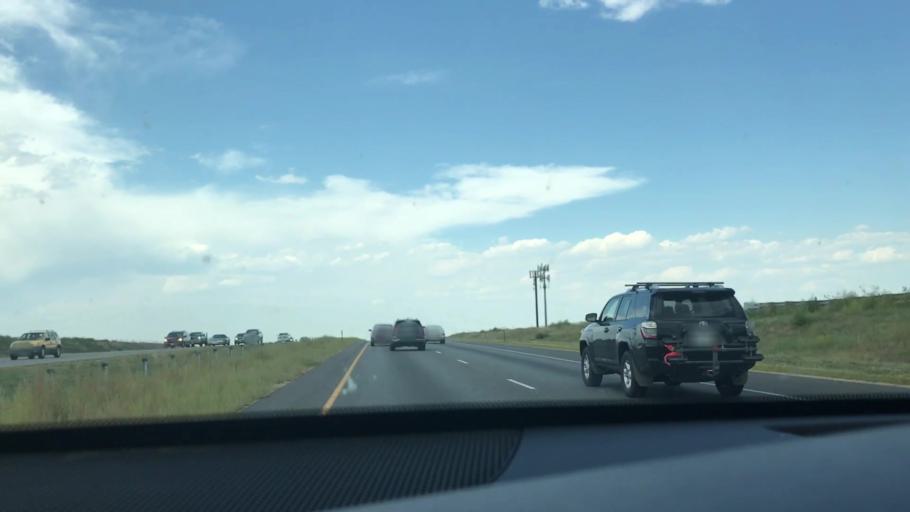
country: US
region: Colorado
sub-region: Weld County
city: Mead
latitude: 40.2687
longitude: -104.9799
